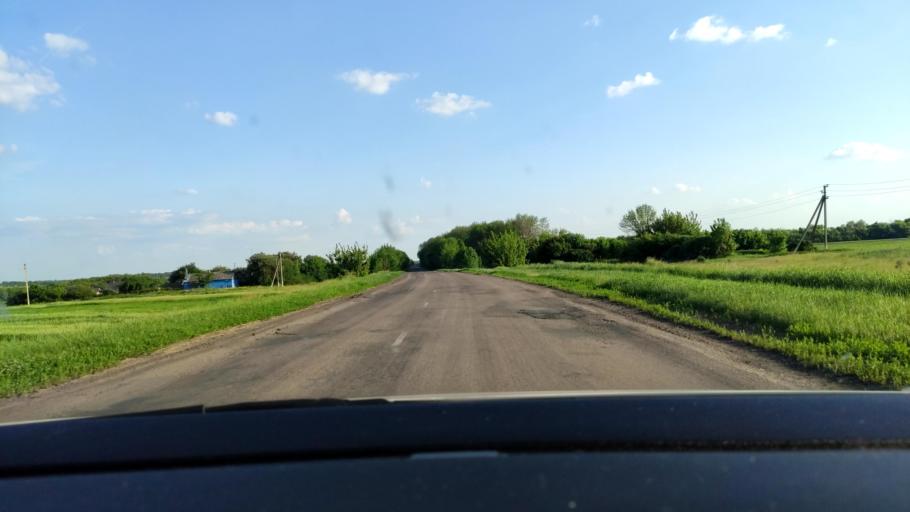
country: RU
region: Voronezj
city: Kashirskoye
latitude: 51.5162
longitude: 39.8330
